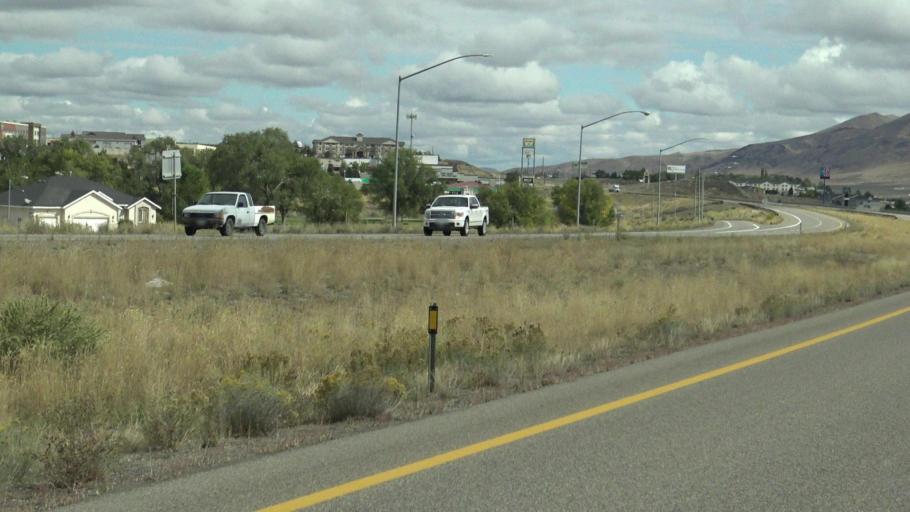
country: US
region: Nevada
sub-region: Elko County
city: Elko
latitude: 40.8489
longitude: -115.7537
